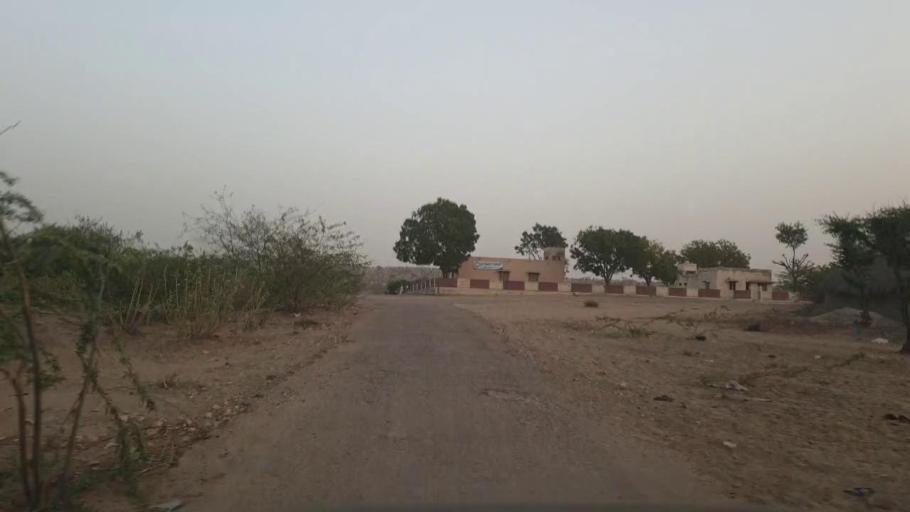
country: PK
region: Sindh
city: Chor
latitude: 25.4997
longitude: 69.8233
